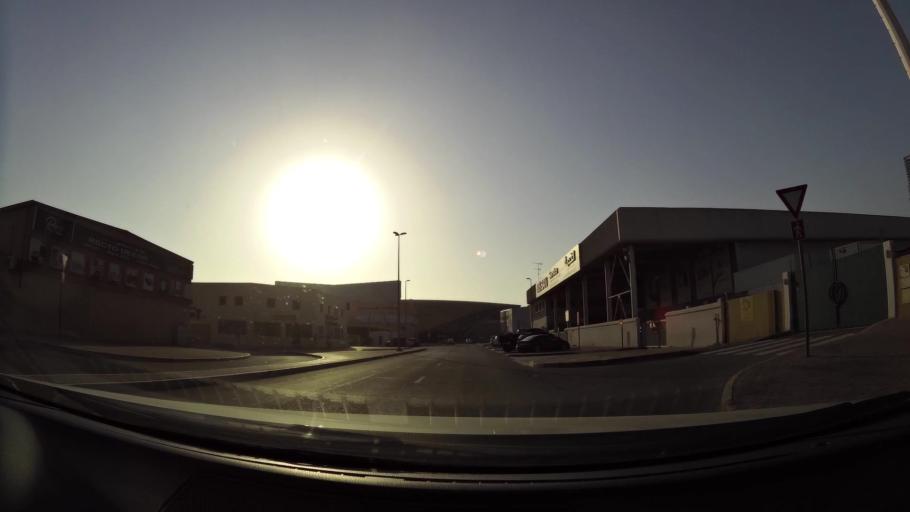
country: AE
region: Dubai
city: Dubai
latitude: 25.1549
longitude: 55.2302
